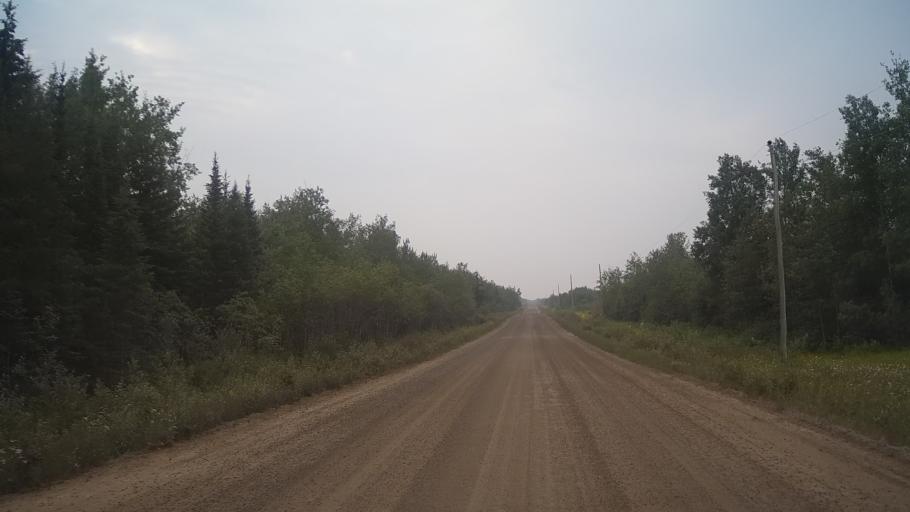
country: CA
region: Ontario
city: Hearst
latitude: 49.6389
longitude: -83.2783
